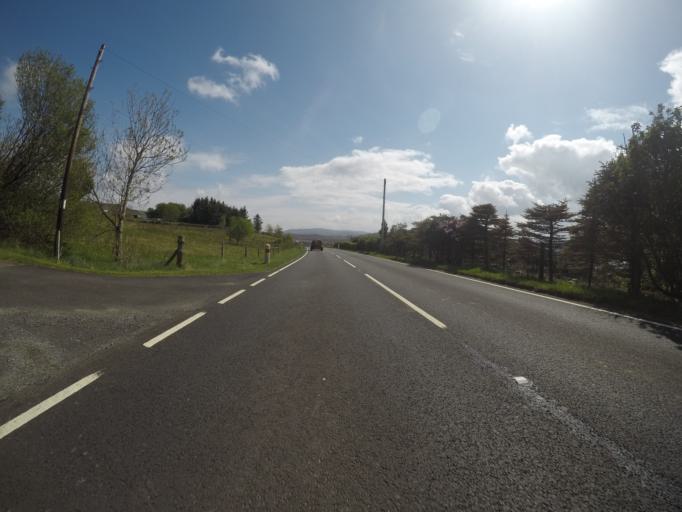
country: GB
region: Scotland
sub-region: Highland
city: Portree
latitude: 57.4931
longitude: -6.3195
